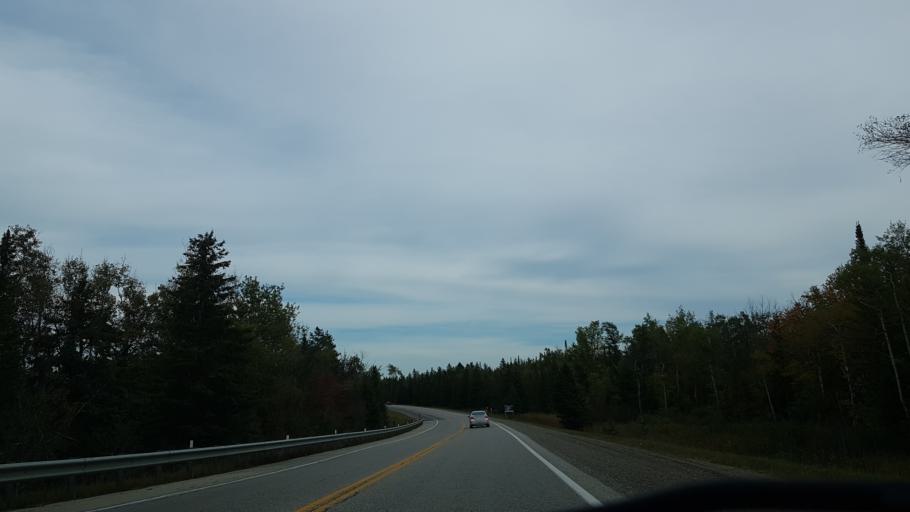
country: CA
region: Ontario
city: Orangeville
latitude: 43.7312
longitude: -80.0958
